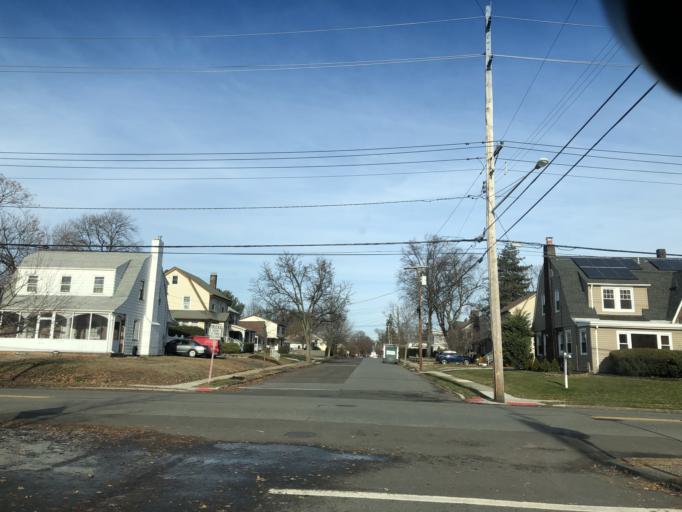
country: US
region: New Jersey
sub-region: Bergen County
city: Fair Lawn
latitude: 40.9254
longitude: -74.1352
